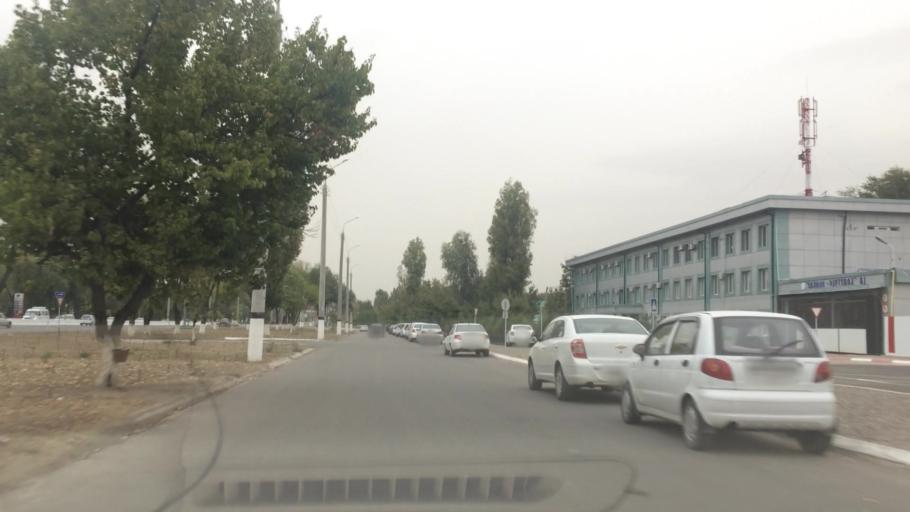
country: UZ
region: Toshkent
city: Salor
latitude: 41.3110
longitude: 69.3467
